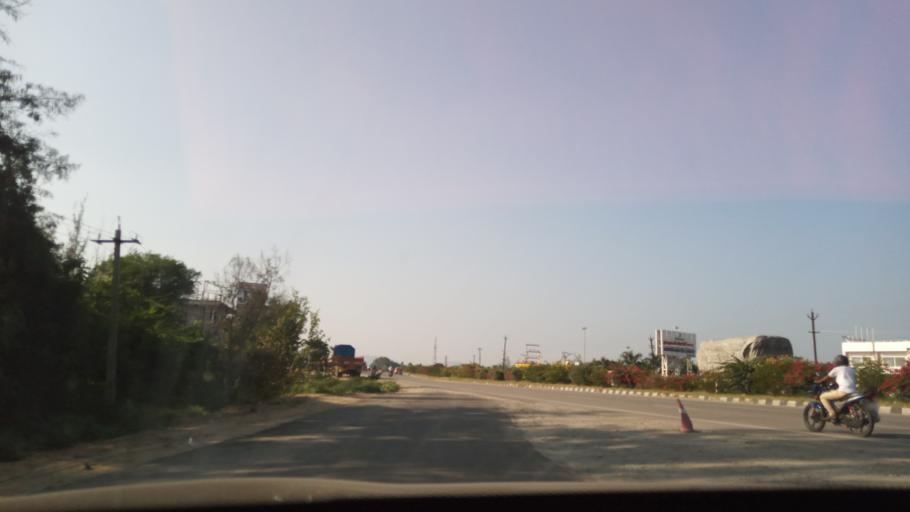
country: IN
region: Tamil Nadu
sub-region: Krishnagiri
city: Krishnagiri
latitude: 12.5540
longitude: 78.1882
